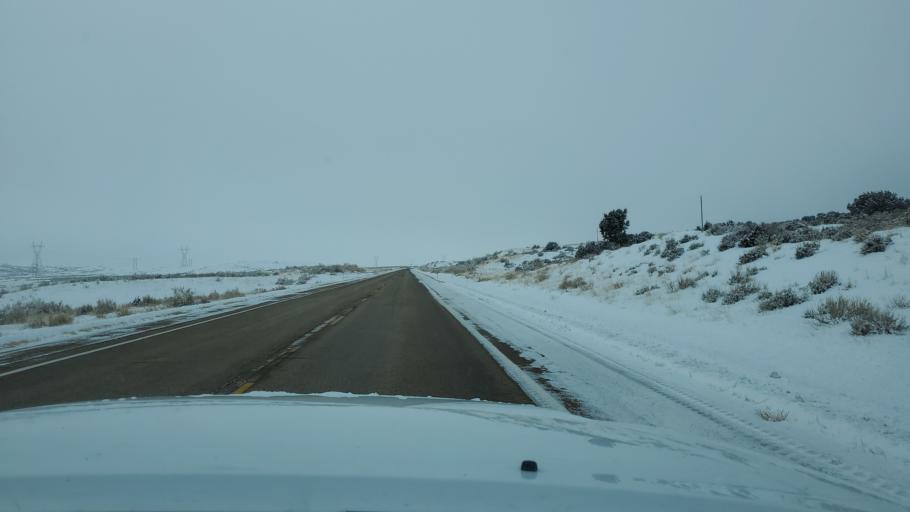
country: US
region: Colorado
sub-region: Rio Blanco County
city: Rangely
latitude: 40.2566
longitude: -108.5810
